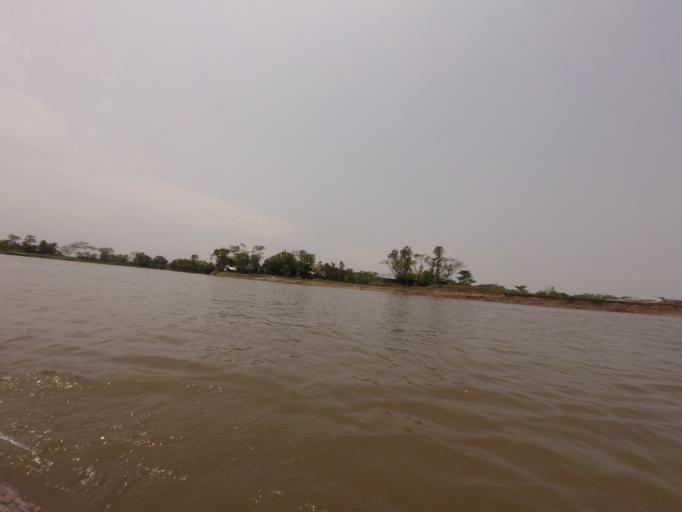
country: BD
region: Sylhet
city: Sylhet
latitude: 25.0094
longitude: 91.9155
